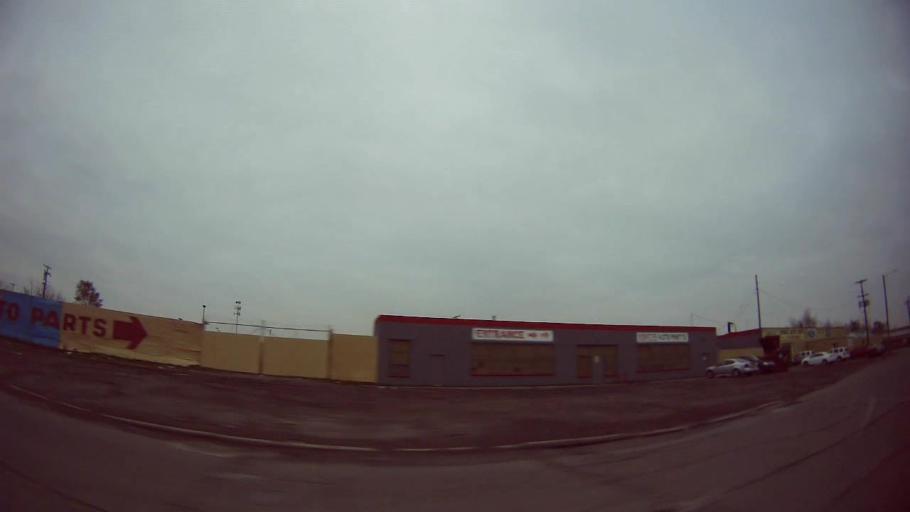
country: US
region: Michigan
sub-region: Wayne County
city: Highland Park
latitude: 42.4184
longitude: -83.0834
